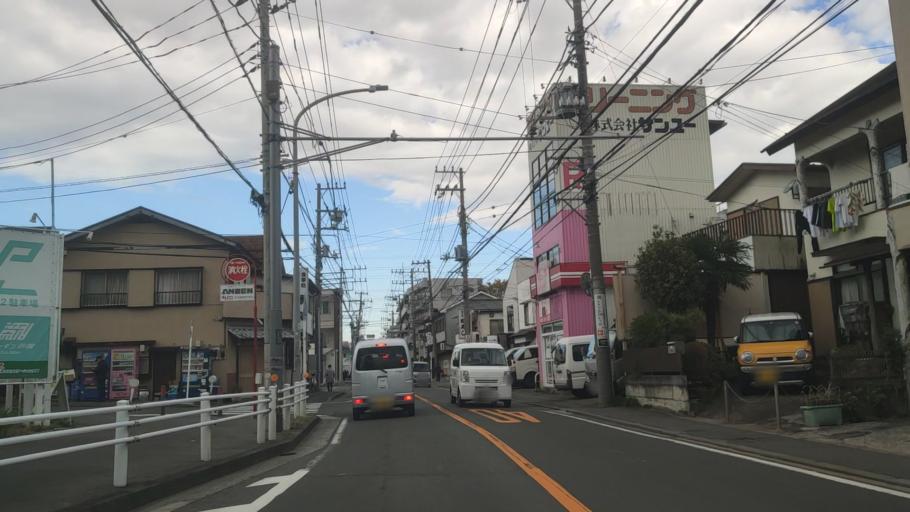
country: JP
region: Kanagawa
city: Fujisawa
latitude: 35.4208
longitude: 139.5351
